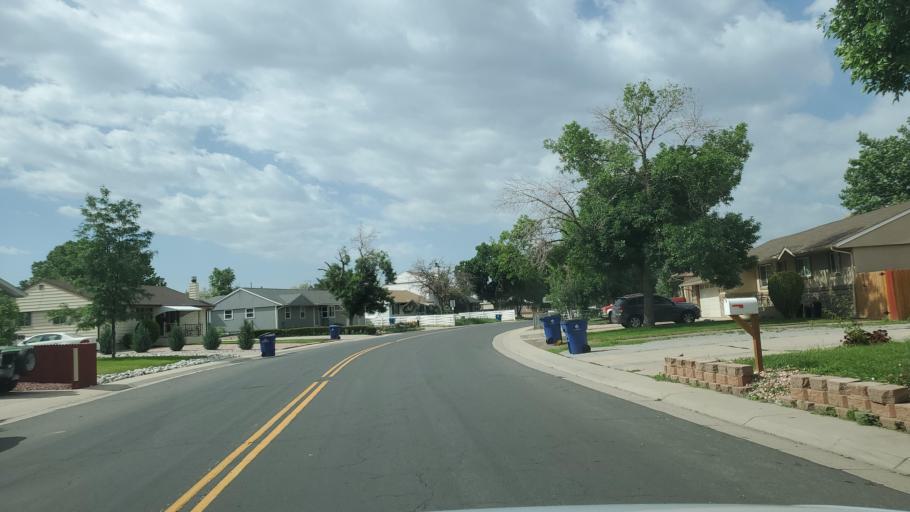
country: US
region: Colorado
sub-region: Adams County
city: Derby
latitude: 39.8413
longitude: -104.9145
